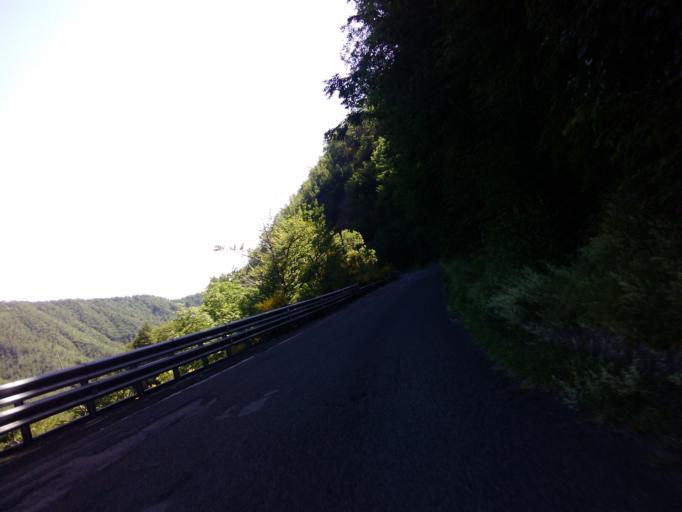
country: IT
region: Tuscany
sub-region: Provincia di Massa-Carrara
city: Comano
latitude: 44.3179
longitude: 10.0911
